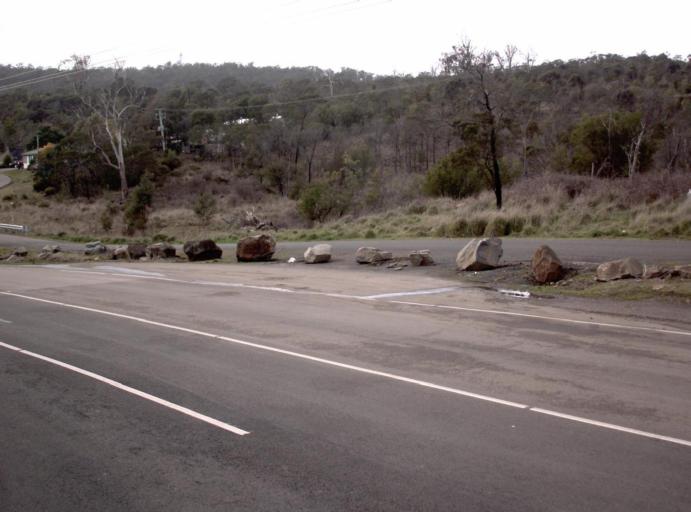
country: AU
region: Tasmania
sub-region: Launceston
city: Newnham
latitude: -41.3992
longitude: 147.1490
